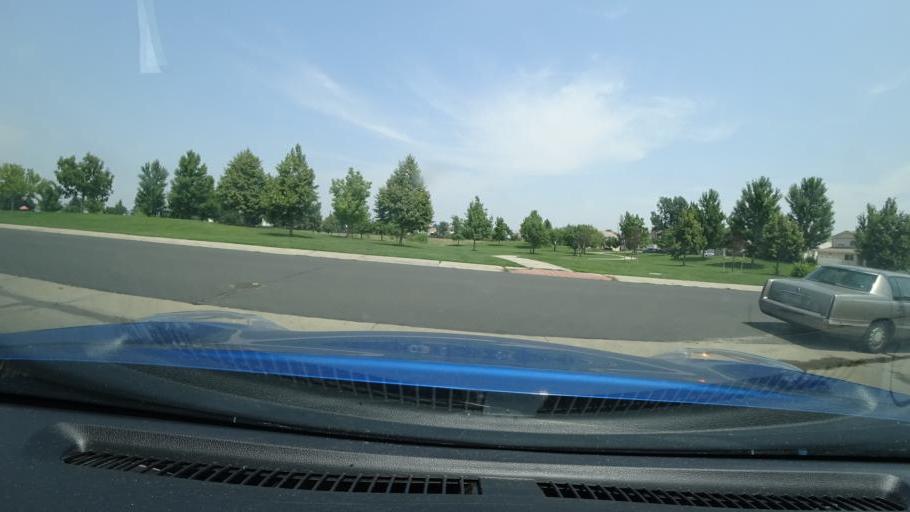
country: US
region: Colorado
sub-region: Adams County
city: Aurora
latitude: 39.7721
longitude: -104.7580
